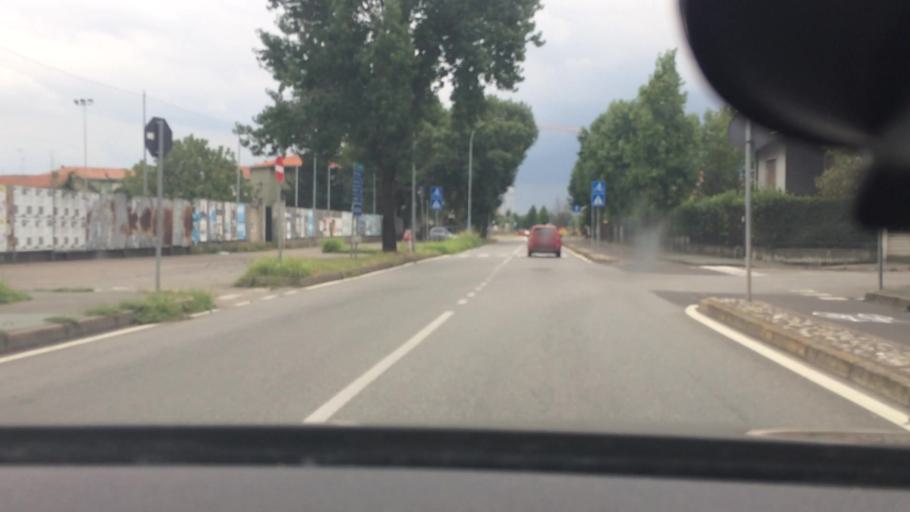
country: IT
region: Lombardy
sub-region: Citta metropolitana di Milano
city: Cerro Maggiore
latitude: 45.5902
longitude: 8.9617
